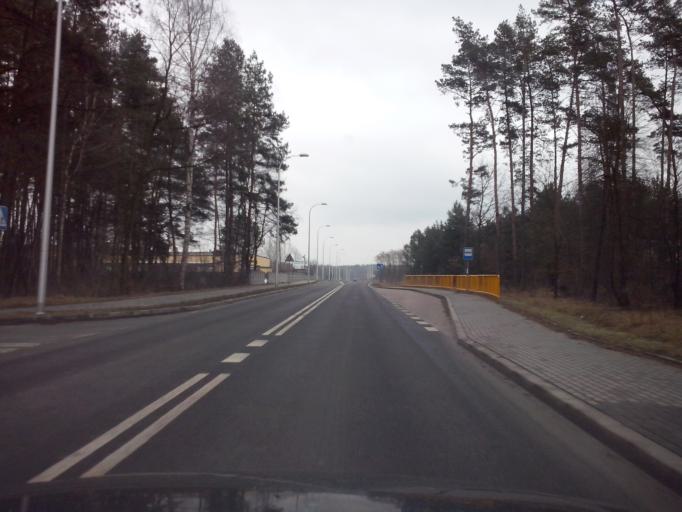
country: PL
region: Subcarpathian Voivodeship
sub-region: Powiat nizanski
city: Przedzel
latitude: 50.5176
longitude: 22.2237
